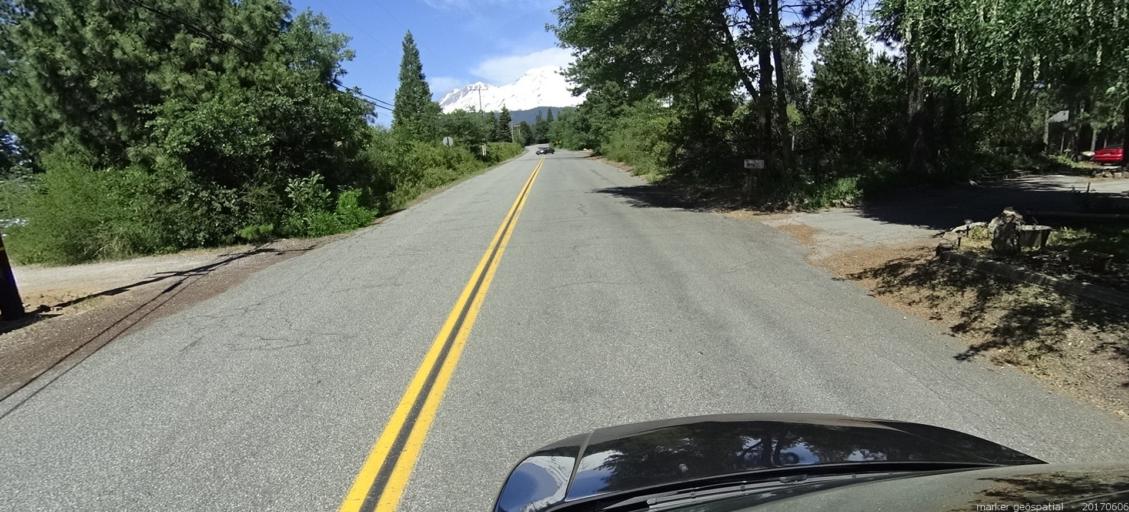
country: US
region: California
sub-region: Siskiyou County
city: Mount Shasta
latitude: 41.2801
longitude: -122.3035
